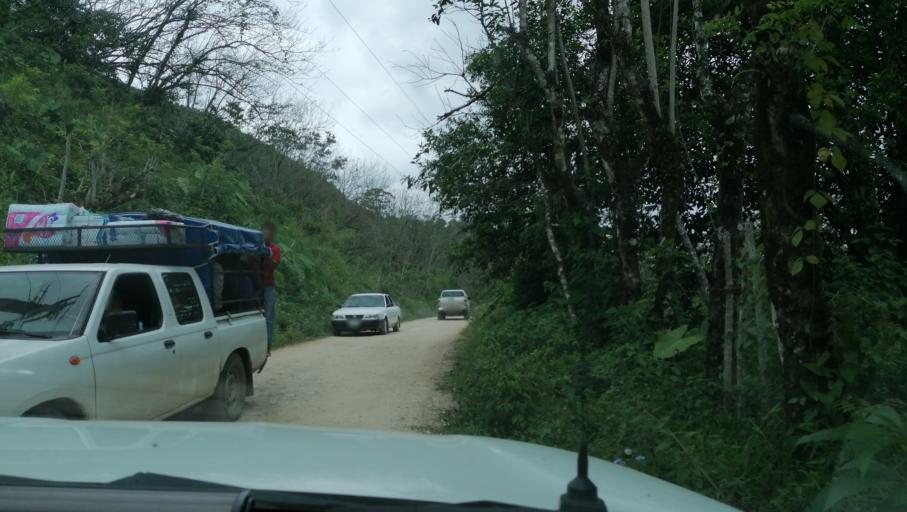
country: MX
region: Chiapas
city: Ocotepec
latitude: 17.2744
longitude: -93.2259
